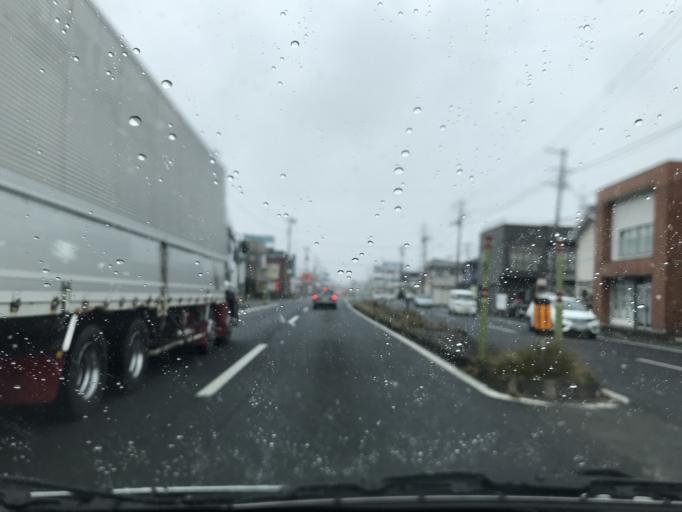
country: JP
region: Iwate
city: Kitakami
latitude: 39.2897
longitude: 141.1044
